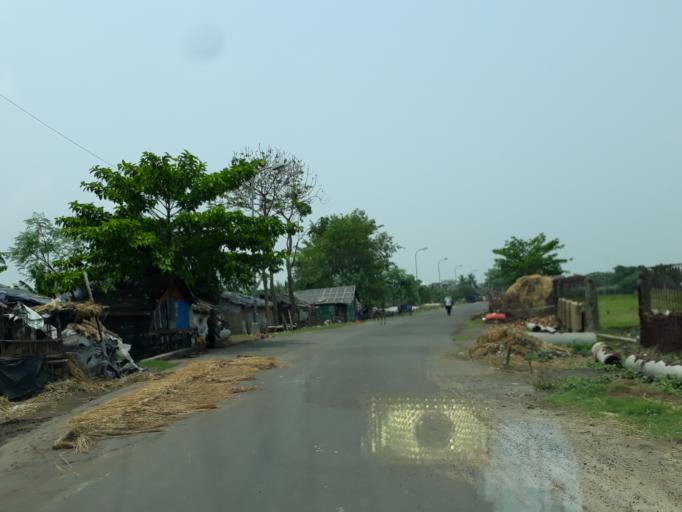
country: IN
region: West Bengal
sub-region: Purba Medinipur
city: Haldia
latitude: 22.0590
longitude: 88.0783
